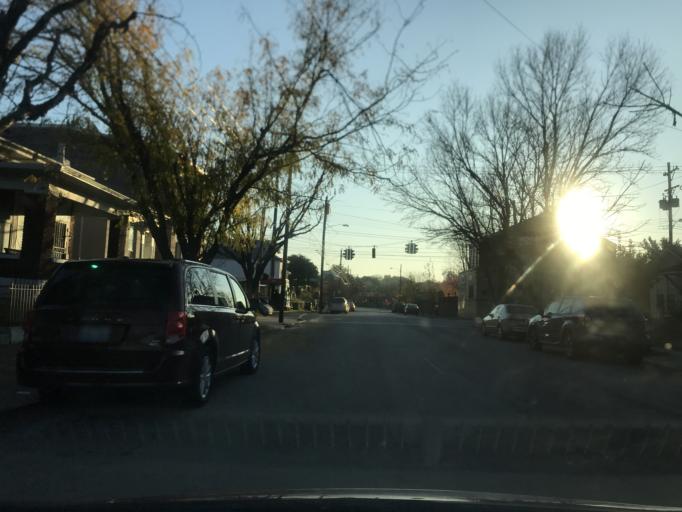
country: US
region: Kentucky
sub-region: Jefferson County
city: Louisville
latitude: 38.2500
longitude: -85.7349
